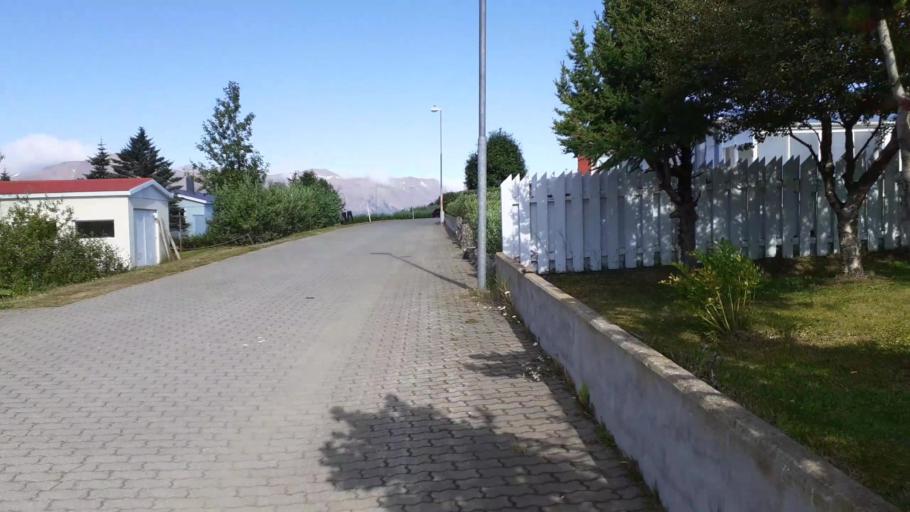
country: IS
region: Northeast
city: Dalvik
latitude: 65.9810
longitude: -18.3782
